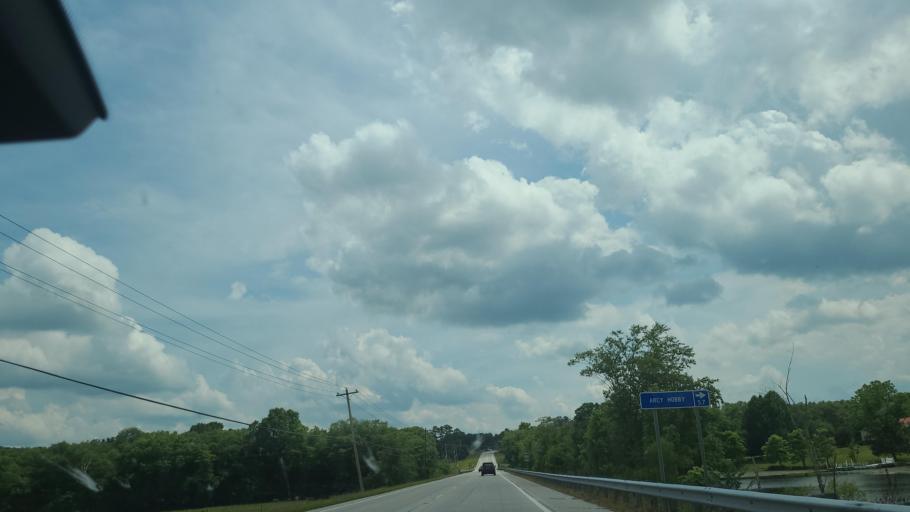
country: US
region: Tennessee
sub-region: Cumberland County
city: Lake Tansi
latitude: 35.8090
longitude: -85.0206
